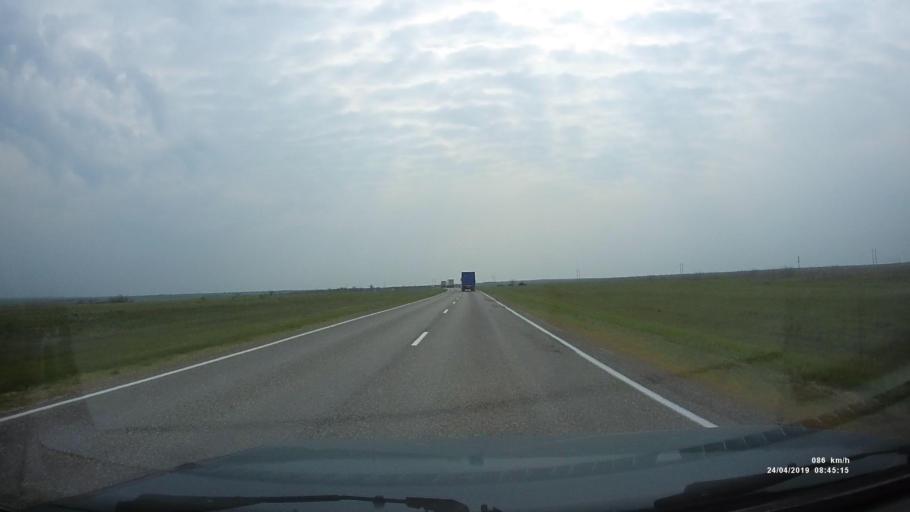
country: RU
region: Kalmykiya
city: Arshan'
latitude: 46.2366
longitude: 44.0574
